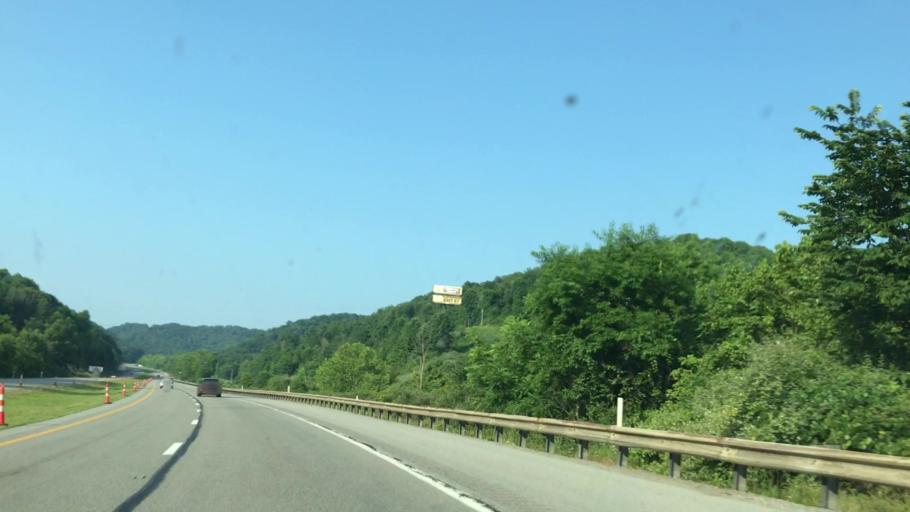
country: US
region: West Virginia
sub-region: Lewis County
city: Weston
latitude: 39.0129
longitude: -80.4944
